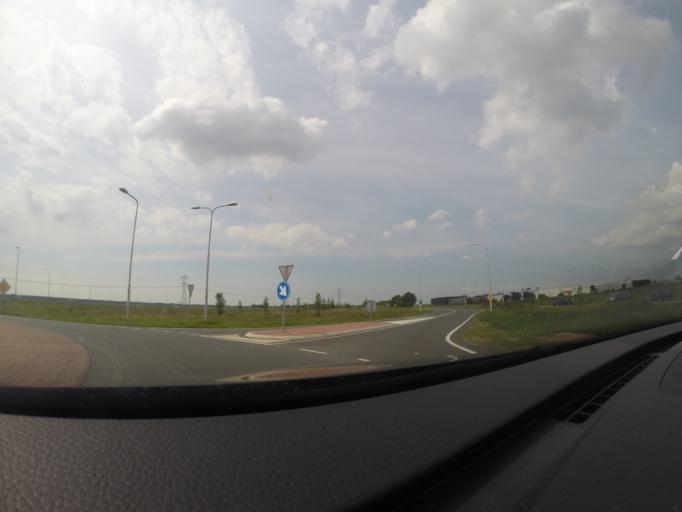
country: NL
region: Flevoland
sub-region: Gemeente Noordoostpolder
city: Ens
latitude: 52.6401
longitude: 5.8175
